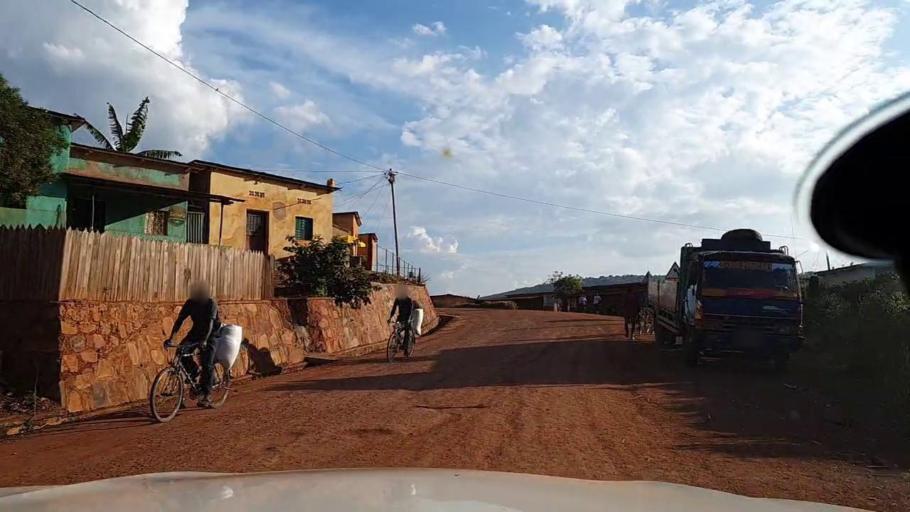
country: RW
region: Kigali
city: Kigali
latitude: -1.9287
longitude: 29.9928
